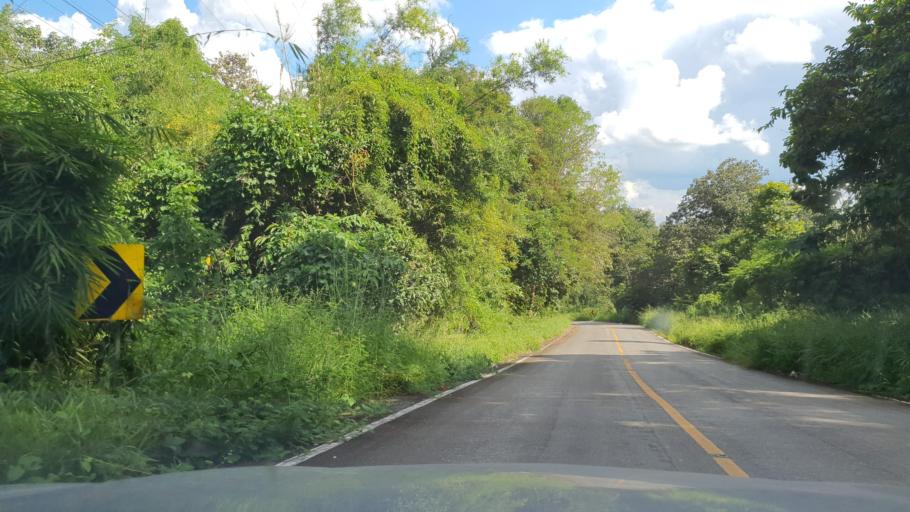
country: TH
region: Chiang Rai
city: Wiang Pa Pao
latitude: 19.3316
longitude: 99.4618
